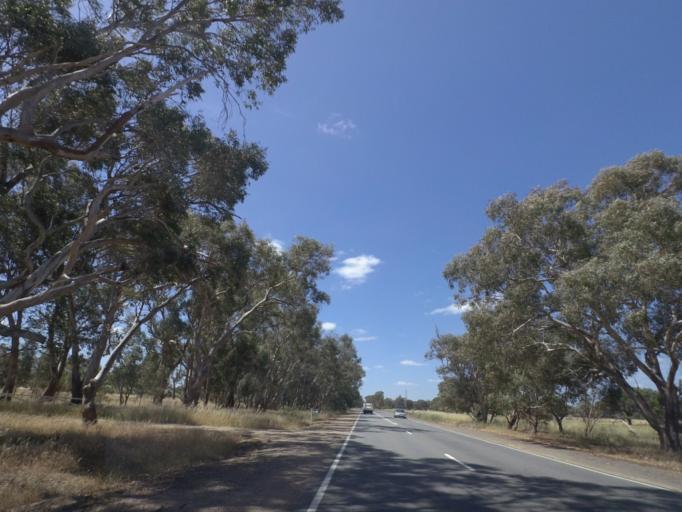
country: AU
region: Victoria
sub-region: Wangaratta
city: Wangaratta
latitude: -36.4140
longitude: 146.2666
